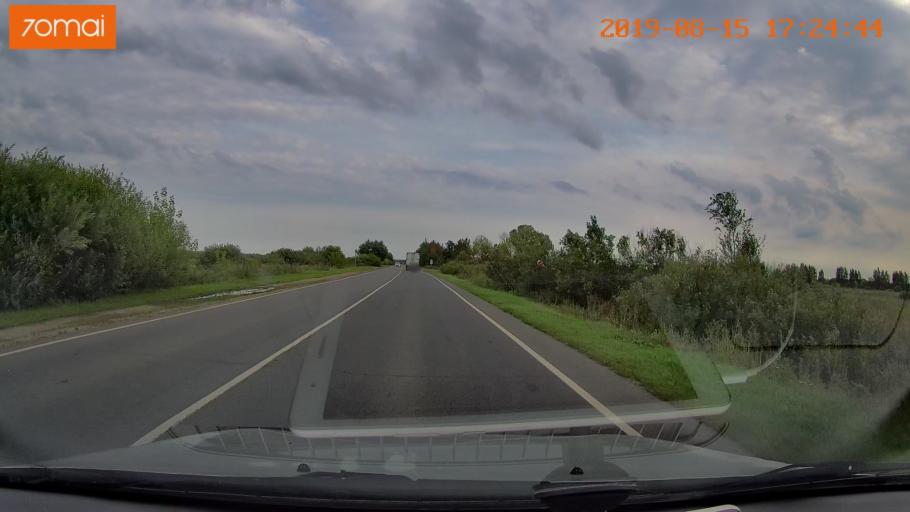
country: RU
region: Moskovskaya
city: Ashitkovo
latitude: 55.3832
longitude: 38.5575
